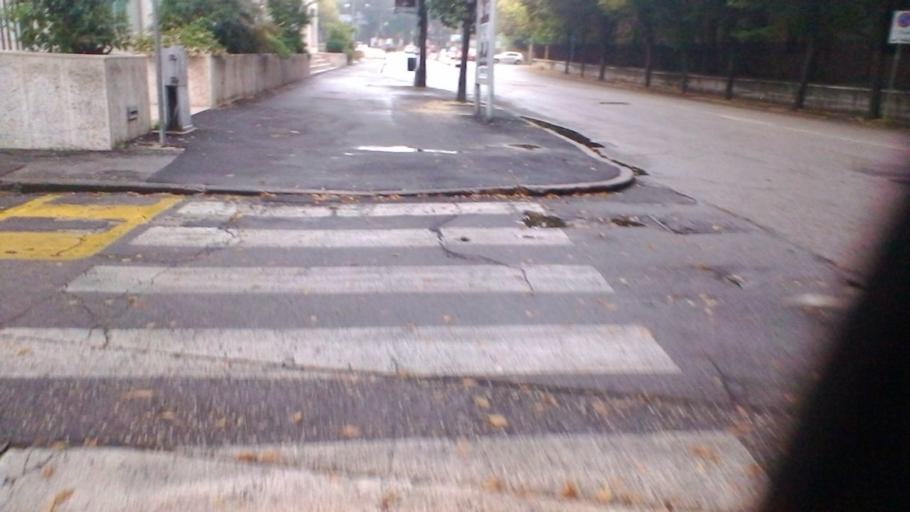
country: IT
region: Veneto
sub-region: Provincia di Verona
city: Verona
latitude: 45.4313
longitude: 10.9952
